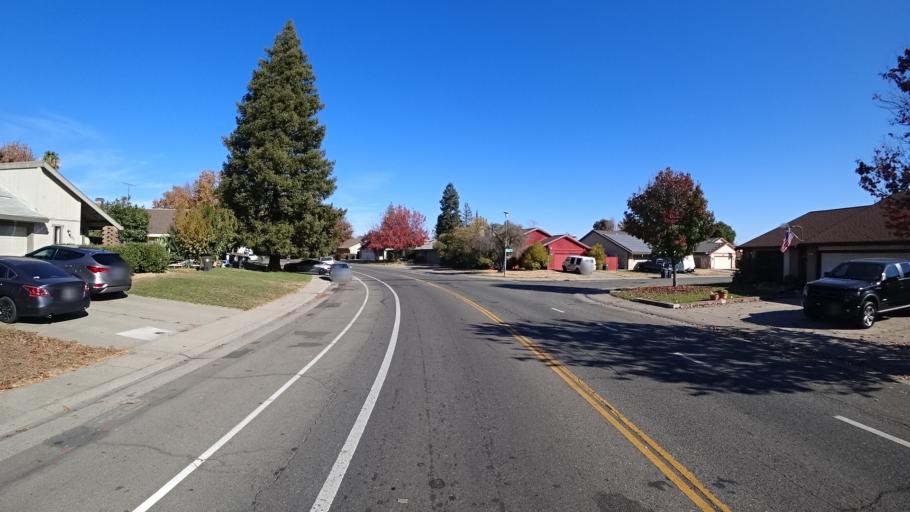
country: US
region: California
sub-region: Sacramento County
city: Antelope
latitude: 38.7105
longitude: -121.3117
